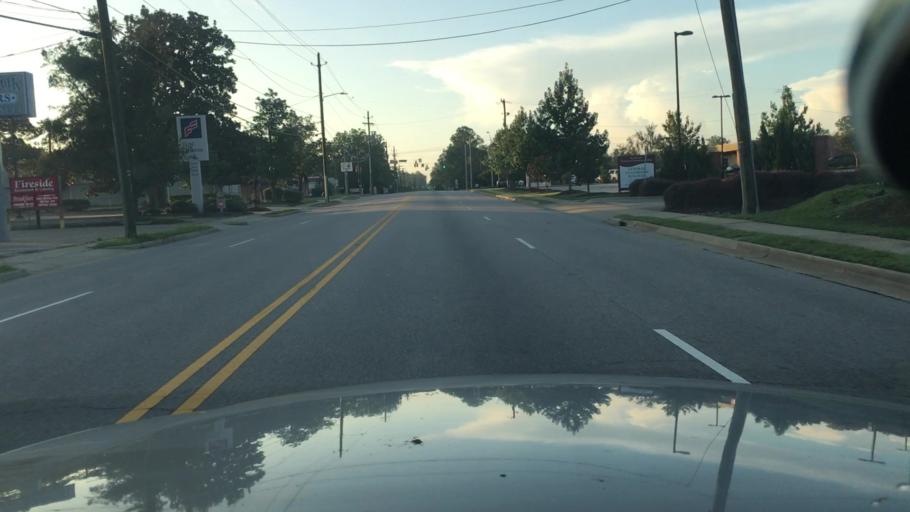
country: US
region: North Carolina
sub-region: Cumberland County
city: Fayetteville
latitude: 35.0718
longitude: -78.9256
